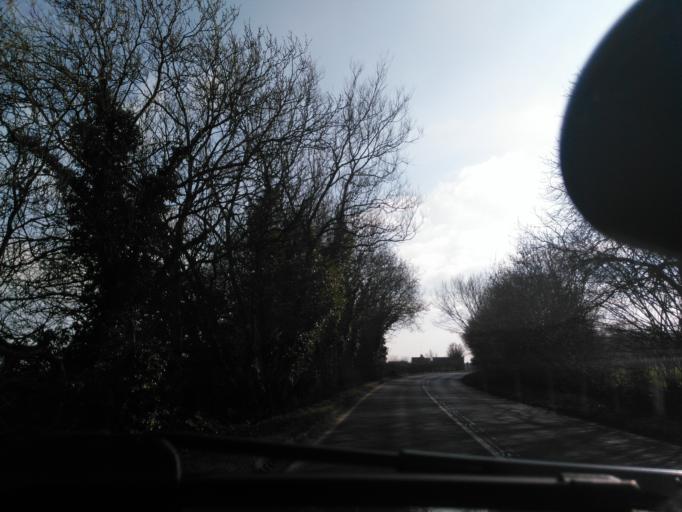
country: GB
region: England
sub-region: Wiltshire
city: Norton
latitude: 51.5303
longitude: -2.1247
